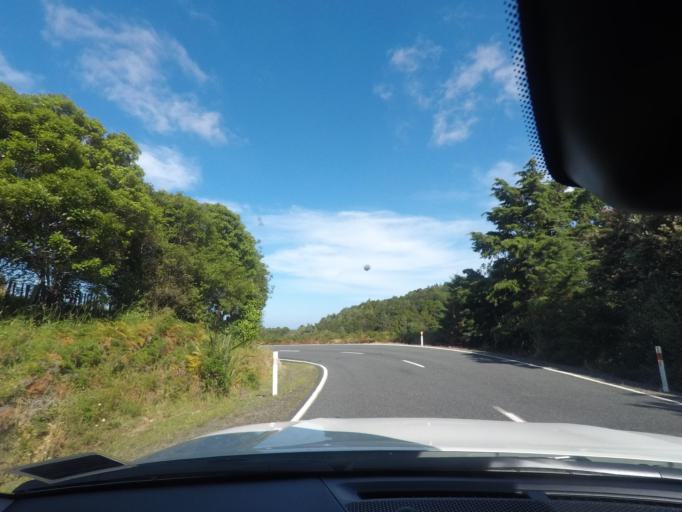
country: NZ
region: Northland
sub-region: Whangarei
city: Ngunguru
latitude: -35.6715
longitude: 174.4694
